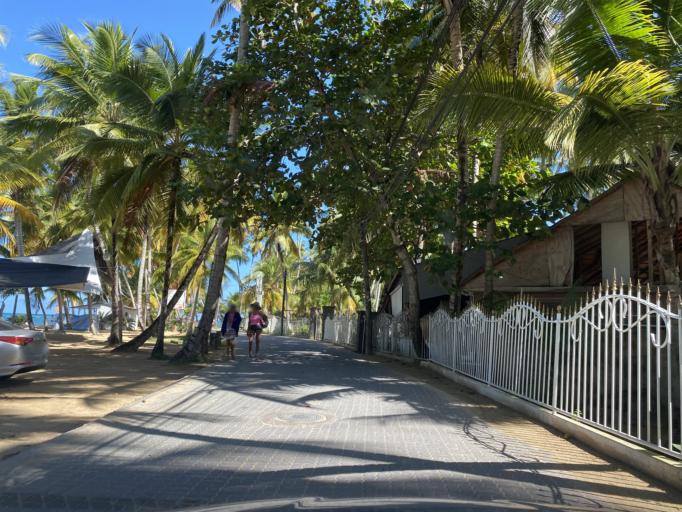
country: DO
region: Samana
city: Las Terrenas
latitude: 19.3258
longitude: -69.5487
